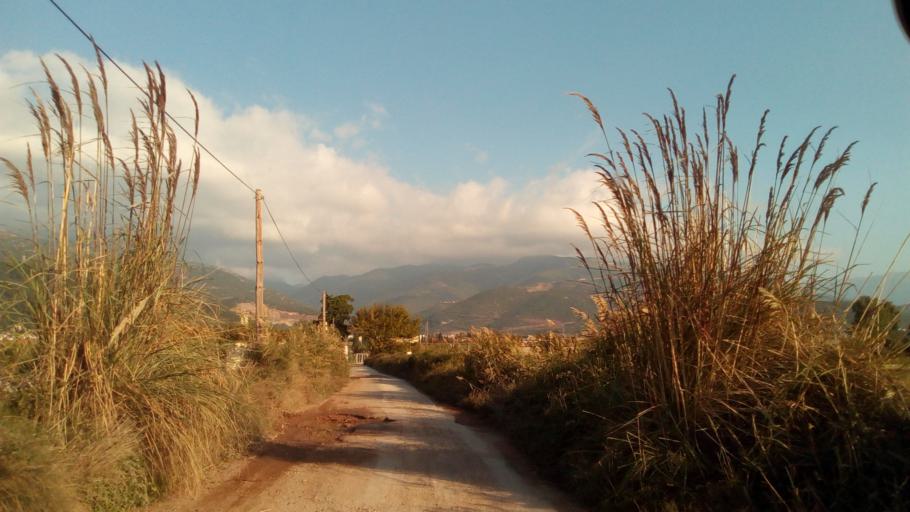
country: GR
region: West Greece
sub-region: Nomos Aitolias kai Akarnanias
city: Nafpaktos
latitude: 38.3857
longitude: 21.8500
